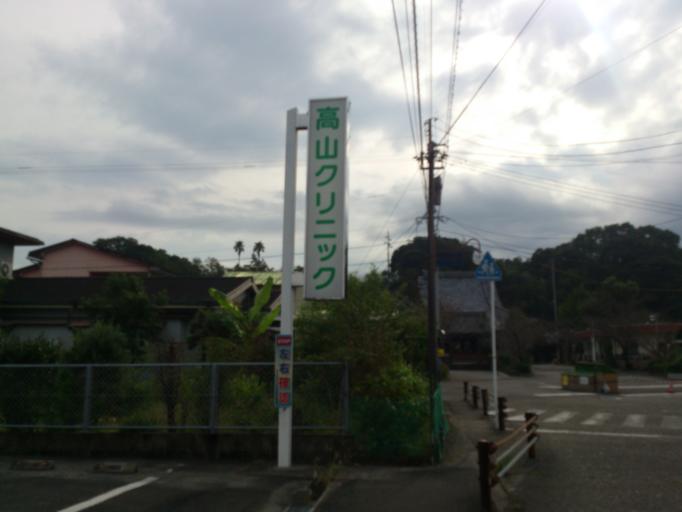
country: JP
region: Kagoshima
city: Kanoya
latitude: 31.3471
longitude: 130.9526
